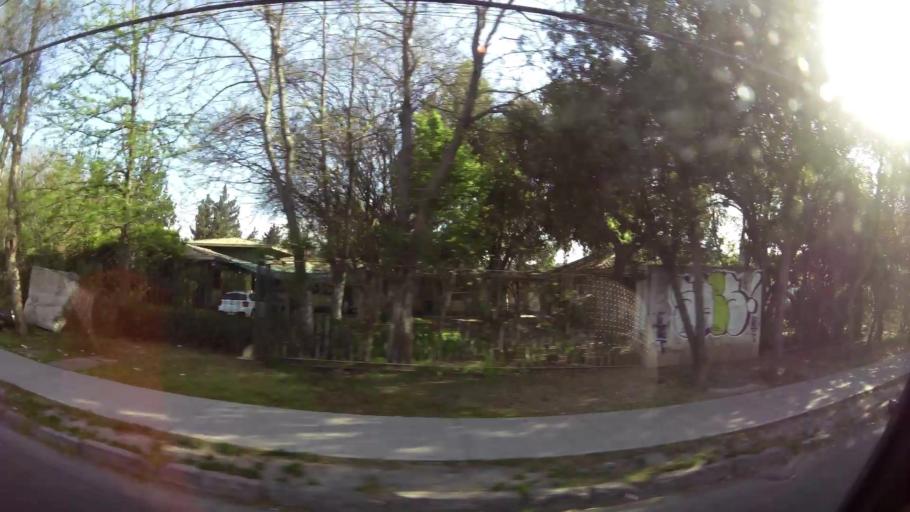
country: CL
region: Santiago Metropolitan
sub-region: Provincia de Santiago
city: Lo Prado
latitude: -33.4382
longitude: -70.7478
